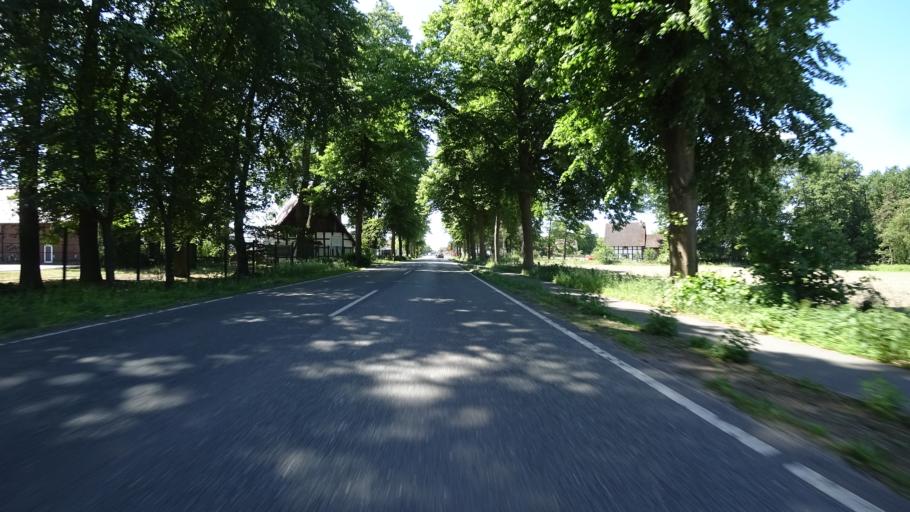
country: DE
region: North Rhine-Westphalia
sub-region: Regierungsbezirk Detmold
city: Guetersloh
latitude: 51.9233
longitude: 8.4017
